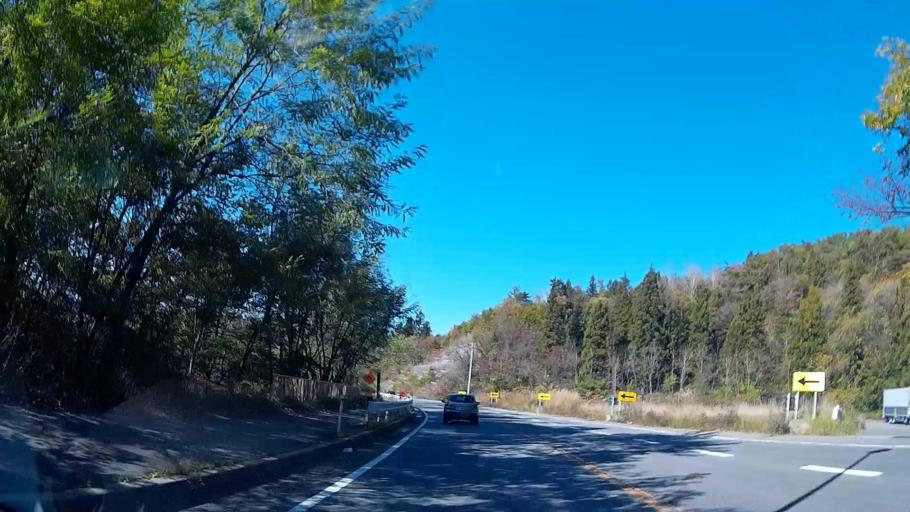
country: JP
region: Nagano
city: Okaya
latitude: 36.0906
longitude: 138.0241
